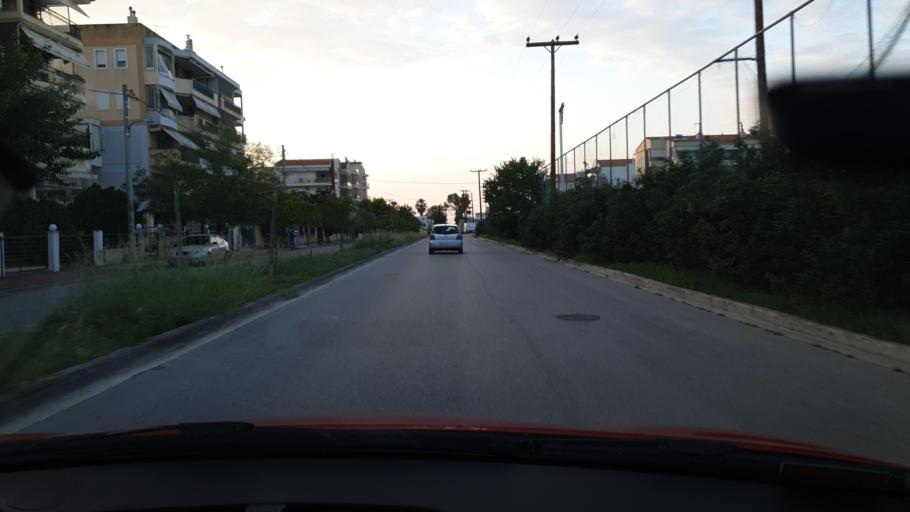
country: GR
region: Central Macedonia
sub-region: Nomos Thessalonikis
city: Peraia
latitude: 40.5096
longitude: 22.9361
